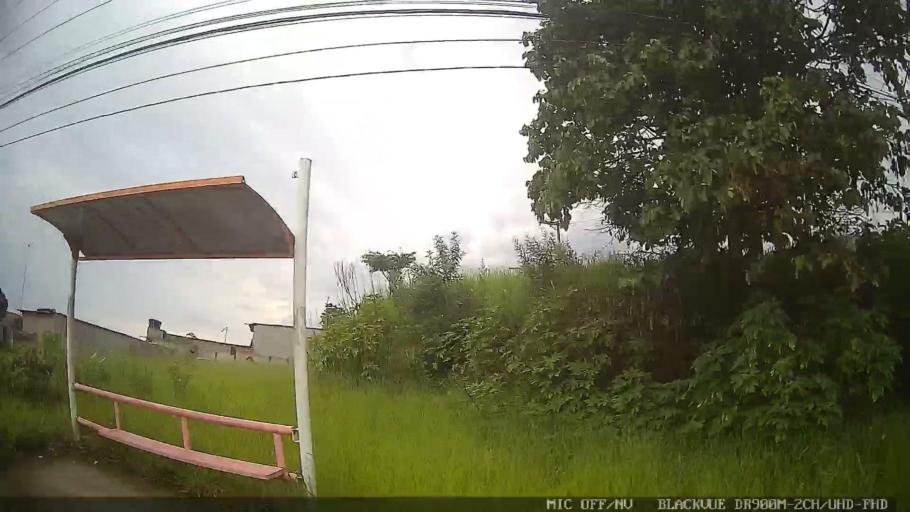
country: BR
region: Sao Paulo
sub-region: Aruja
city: Aruja
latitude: -23.4492
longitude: -46.2946
